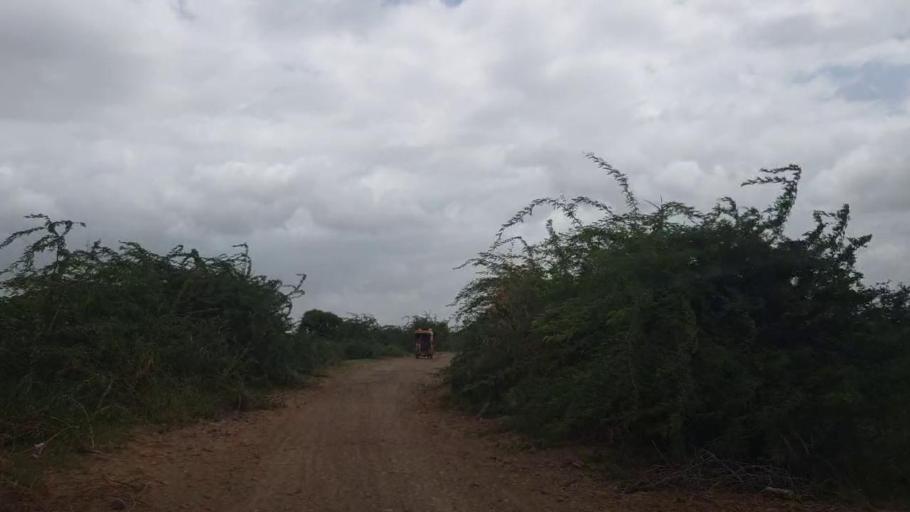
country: PK
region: Sindh
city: Badin
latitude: 24.6420
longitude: 68.9473
